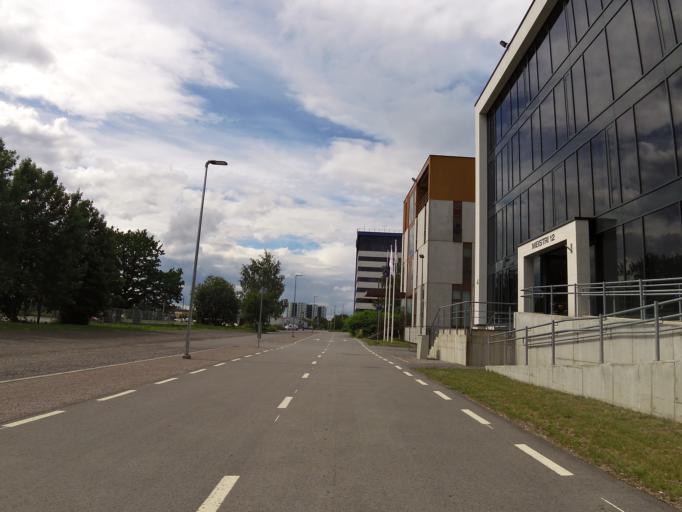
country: EE
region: Harju
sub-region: Saue vald
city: Laagri
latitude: 59.4140
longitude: 24.6638
